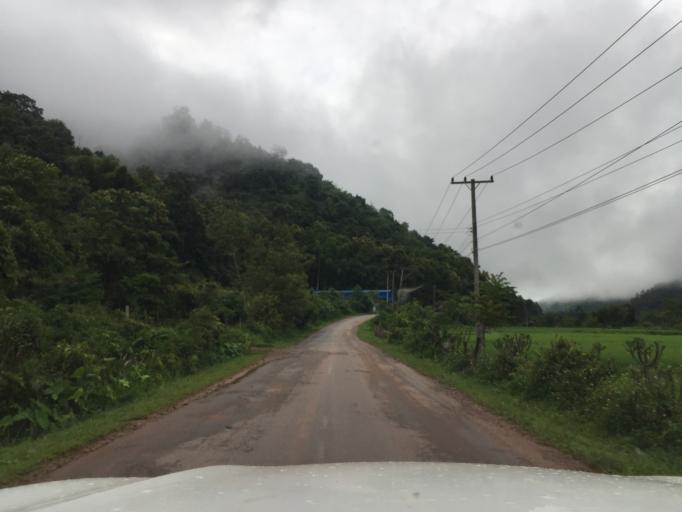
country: LA
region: Oudomxai
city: Muang La
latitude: 20.8383
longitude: 102.1029
